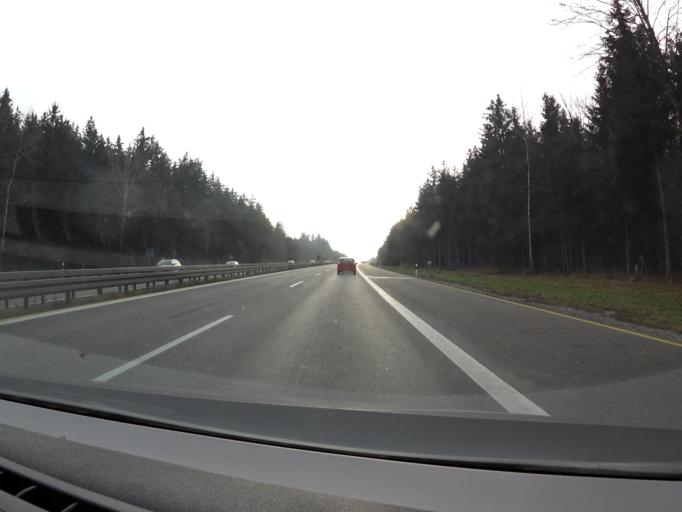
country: DE
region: Bavaria
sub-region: Upper Bavaria
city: Schaftlarn
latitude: 47.9823
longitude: 11.4254
